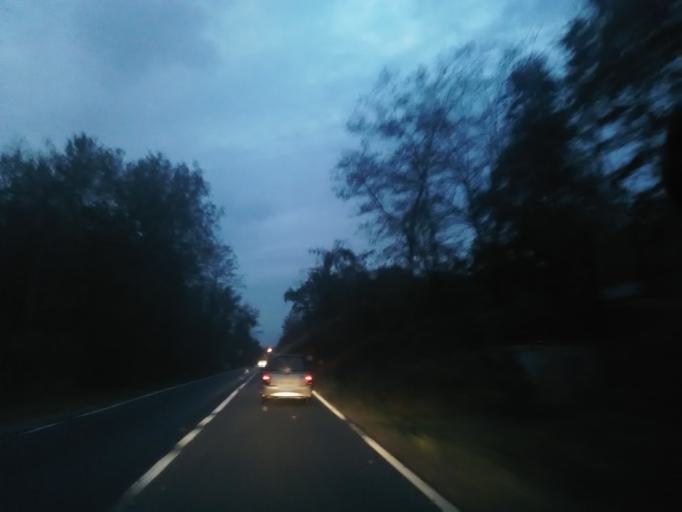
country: IT
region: Piedmont
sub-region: Provincia di Vercelli
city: Lozzolo
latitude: 45.6102
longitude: 8.3364
